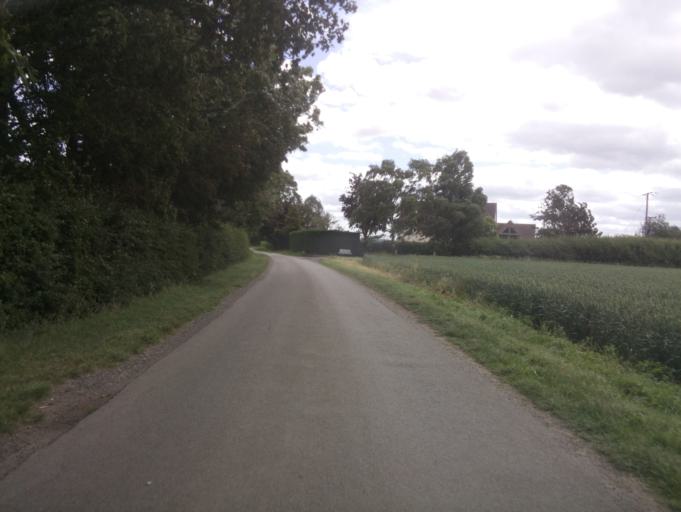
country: GB
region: England
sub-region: Nottinghamshire
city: Cotgrave
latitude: 52.8635
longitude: -1.0615
